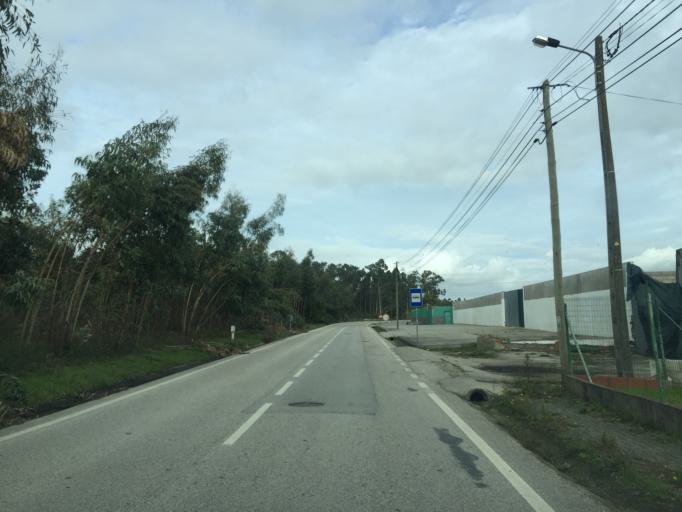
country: PT
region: Coimbra
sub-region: Figueira da Foz
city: Lavos
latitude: 40.0433
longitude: -8.8183
